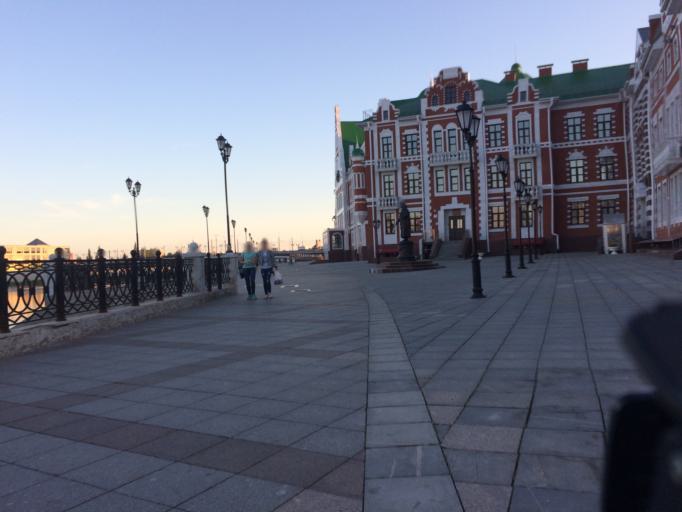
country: RU
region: Mariy-El
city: Yoshkar-Ola
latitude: 56.6316
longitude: 47.8992
